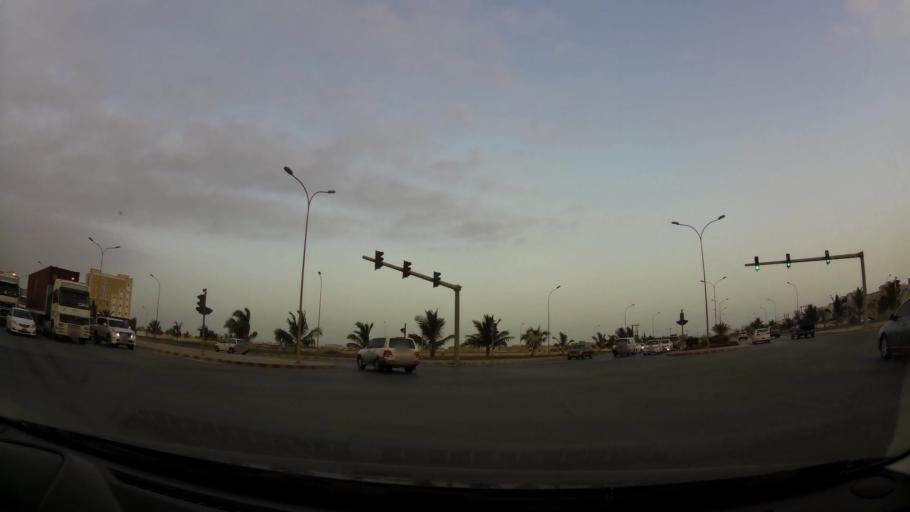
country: OM
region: Zufar
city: Salalah
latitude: 17.0207
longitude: 54.0341
